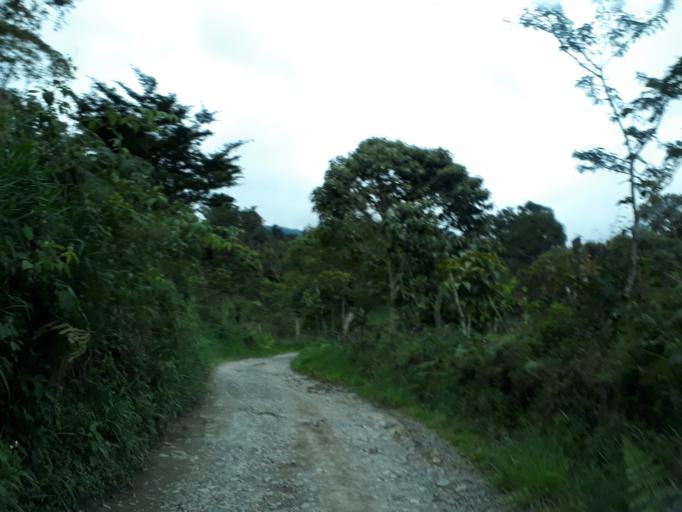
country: CO
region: Boyaca
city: Muzo
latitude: 5.3789
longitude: -74.0904
